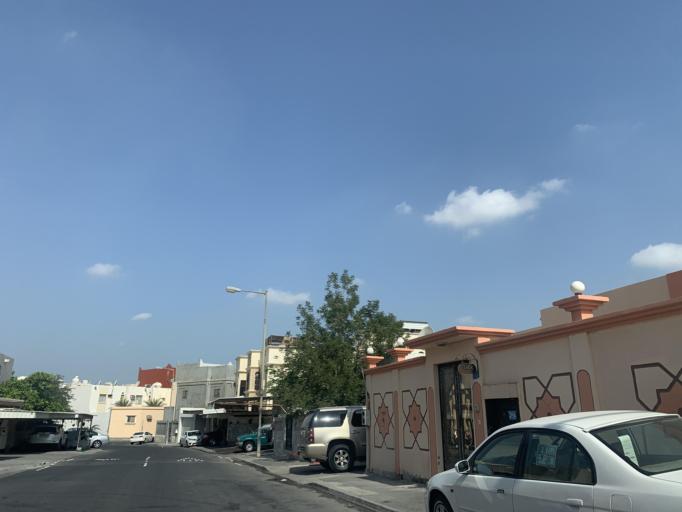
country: BH
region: Central Governorate
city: Madinat Hamad
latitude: 26.1221
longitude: 50.5036
